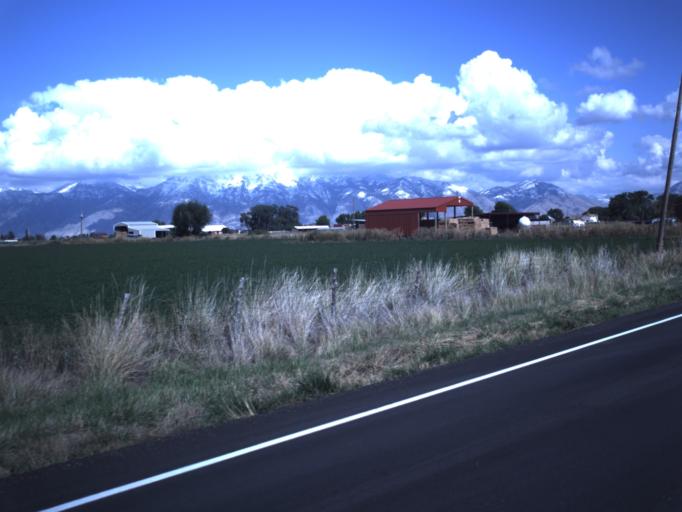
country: US
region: Utah
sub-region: Utah County
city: Benjamin
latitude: 40.0980
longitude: -111.7372
